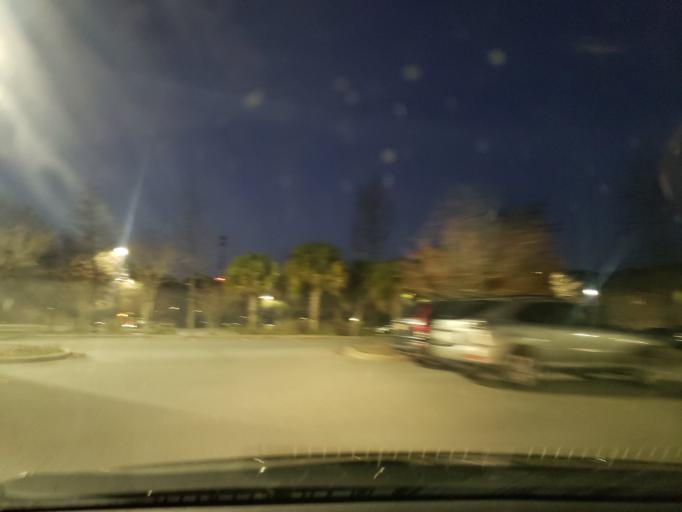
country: US
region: Georgia
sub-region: Chatham County
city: Montgomery
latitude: 31.9757
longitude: -81.1666
